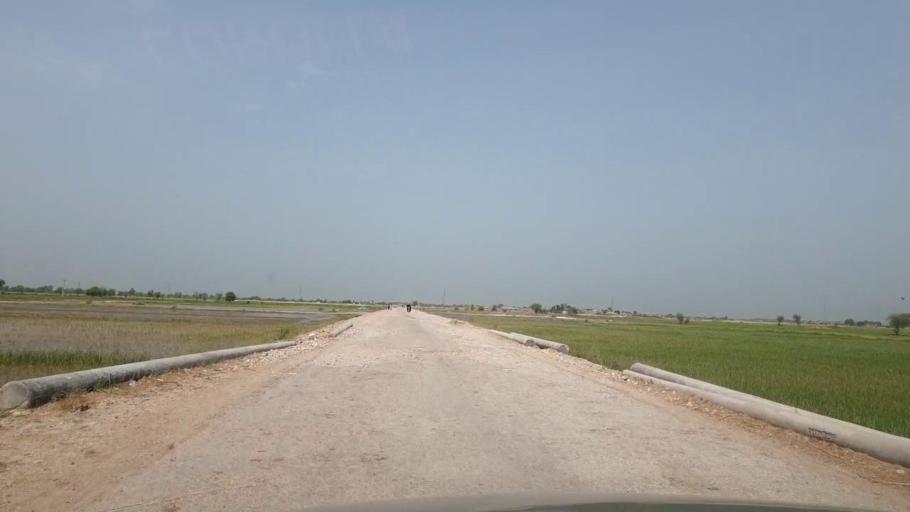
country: PK
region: Sindh
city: Garhi Yasin
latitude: 27.8537
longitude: 68.4358
